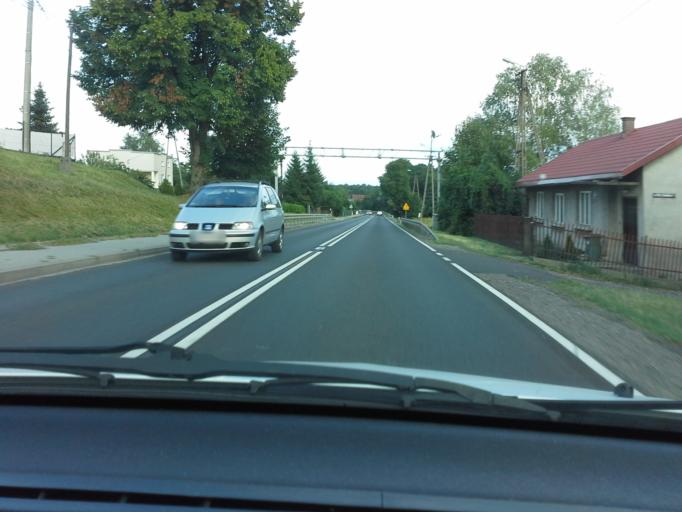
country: PL
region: Lesser Poland Voivodeship
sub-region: Powiat chrzanowski
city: Psary
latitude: 50.1435
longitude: 19.5129
